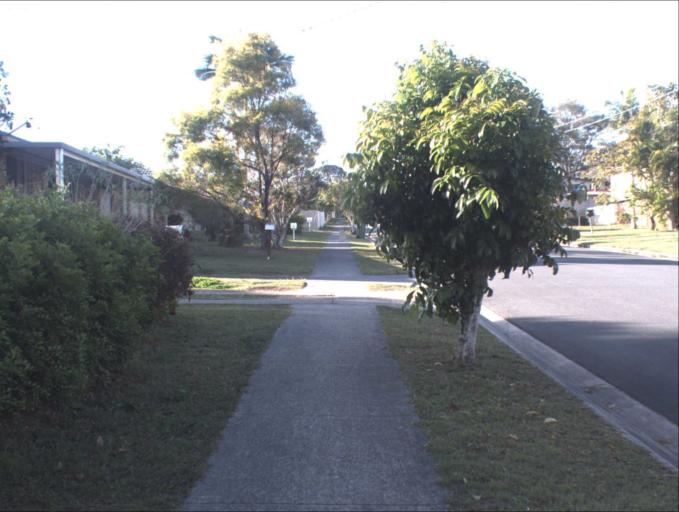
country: AU
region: Queensland
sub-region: Logan
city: Waterford West
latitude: -27.6852
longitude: 153.1015
